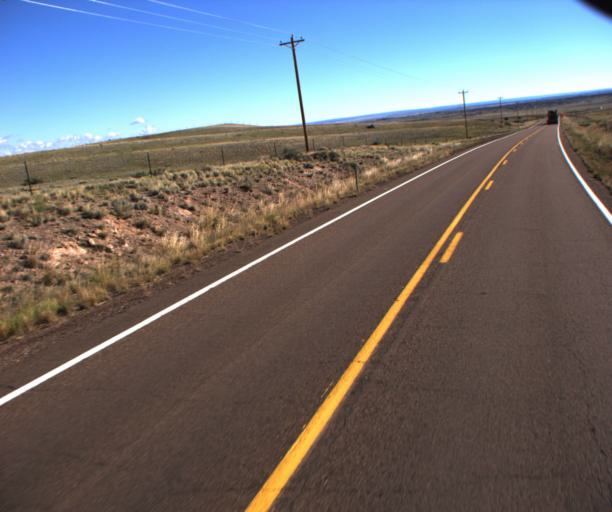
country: US
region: Arizona
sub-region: Apache County
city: Saint Johns
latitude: 34.5078
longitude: -109.4745
